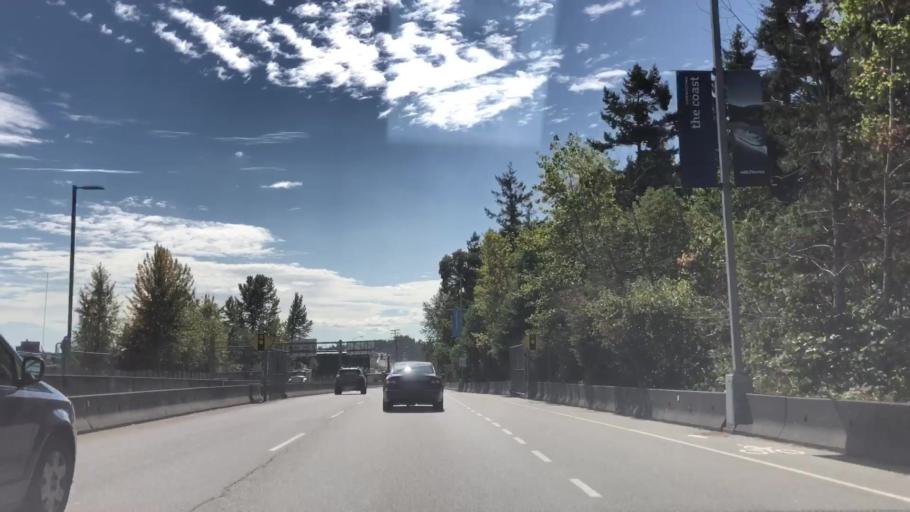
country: CA
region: British Columbia
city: Nanaimo
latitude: 49.1575
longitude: -123.8917
